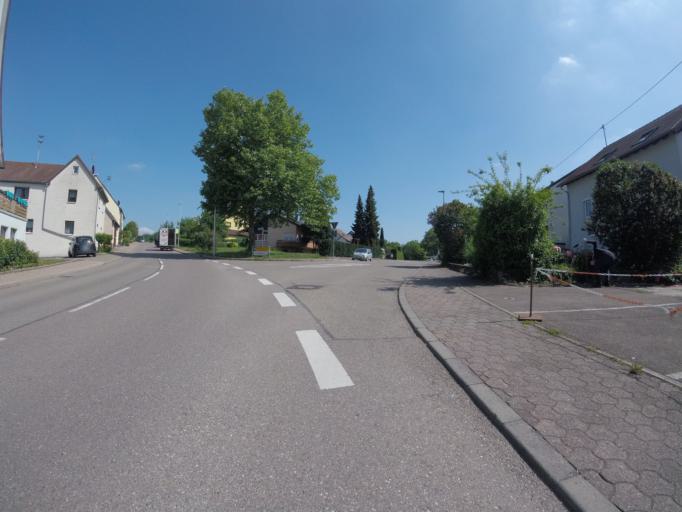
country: DE
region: Baden-Wuerttemberg
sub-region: Regierungsbezirk Stuttgart
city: Steinheim am der Murr
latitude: 48.9775
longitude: 9.2902
